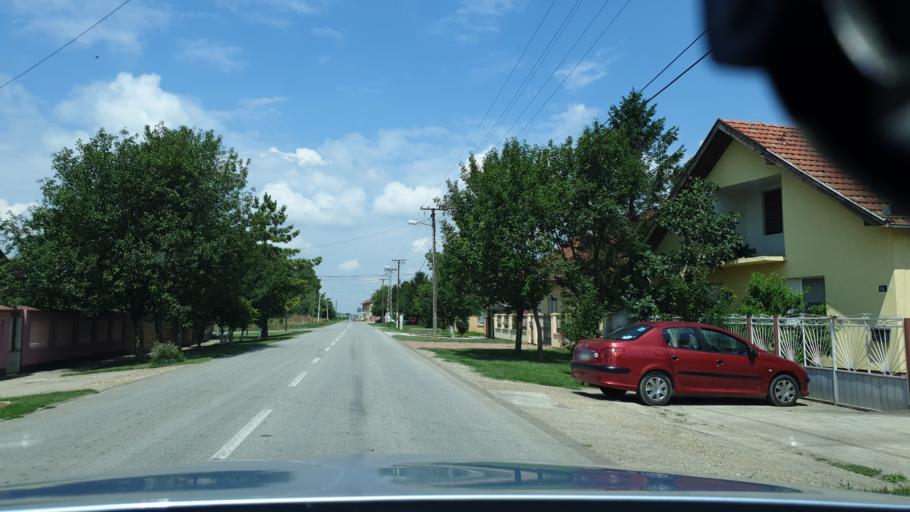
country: RS
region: Autonomna Pokrajina Vojvodina
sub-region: Juznobacki Okrug
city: Kovilj
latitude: 45.2396
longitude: 20.0265
